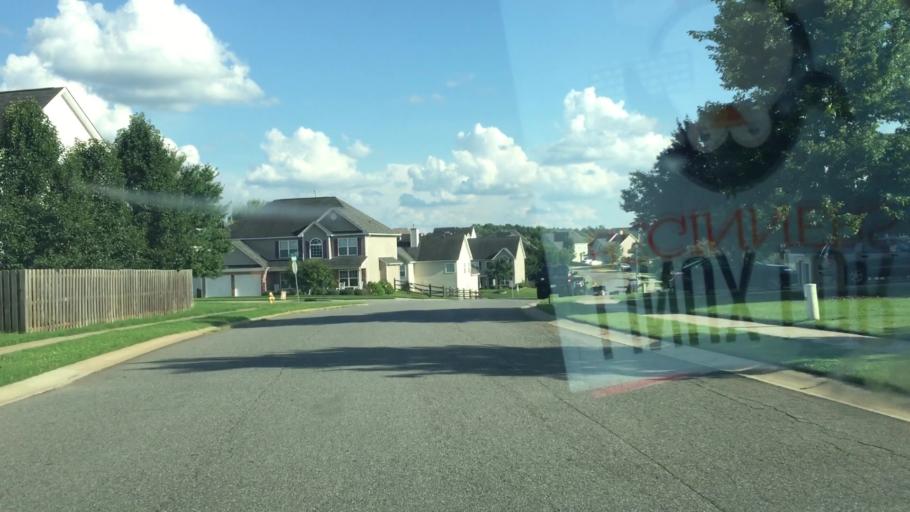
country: US
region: North Carolina
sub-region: Iredell County
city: Mooresville
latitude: 35.5383
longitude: -80.7853
